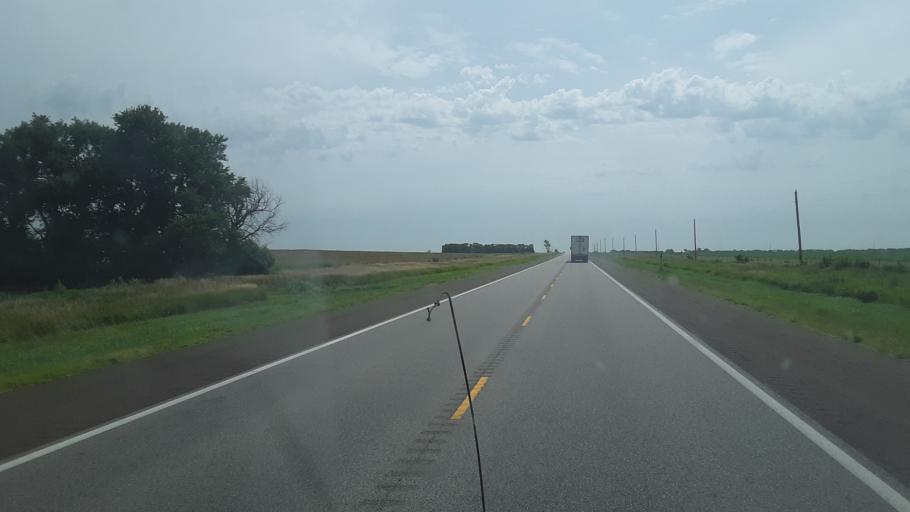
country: US
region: Kansas
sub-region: Reno County
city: Nickerson
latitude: 37.9848
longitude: -98.1341
